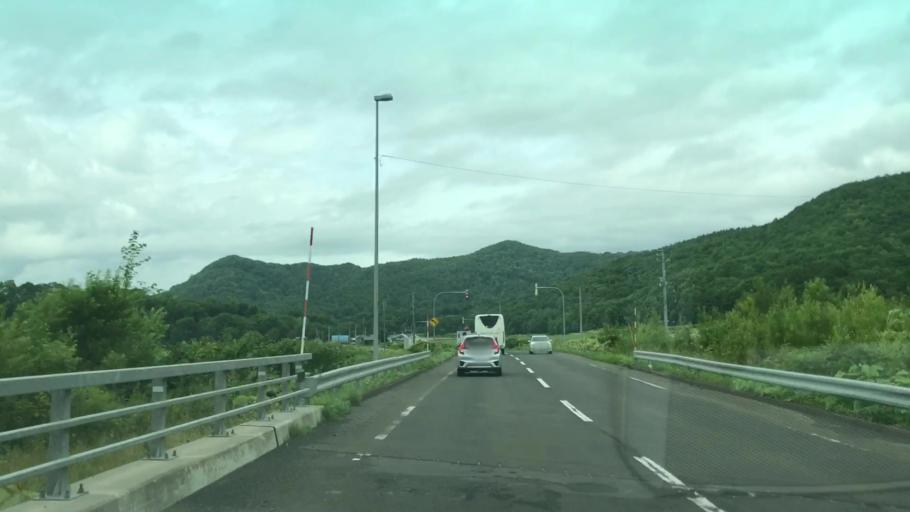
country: JP
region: Hokkaido
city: Niseko Town
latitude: 42.9463
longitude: 140.8390
